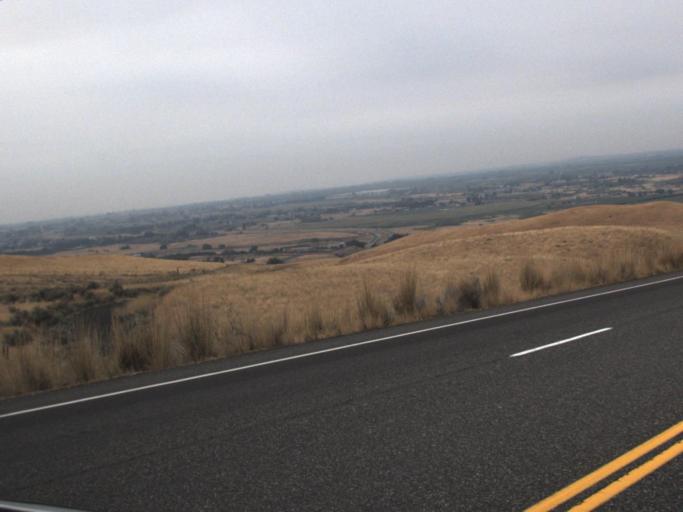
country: US
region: Washington
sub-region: Benton County
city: Prosser
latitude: 46.2034
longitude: -119.7238
